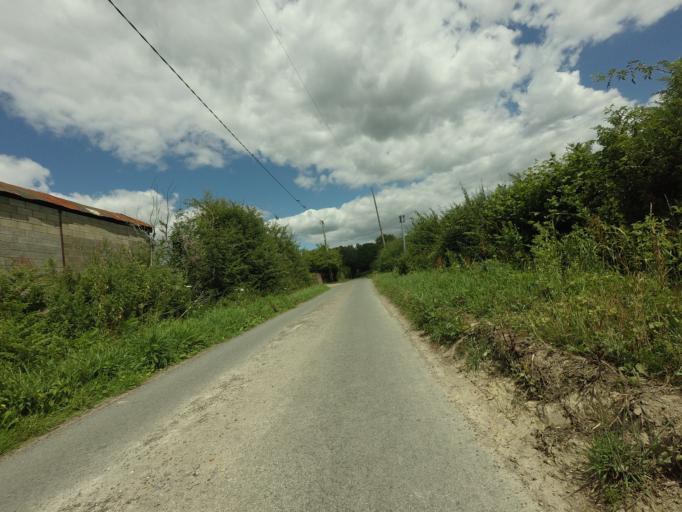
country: GB
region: England
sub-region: East Sussex
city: Hailsham
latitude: 50.8335
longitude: 0.2779
